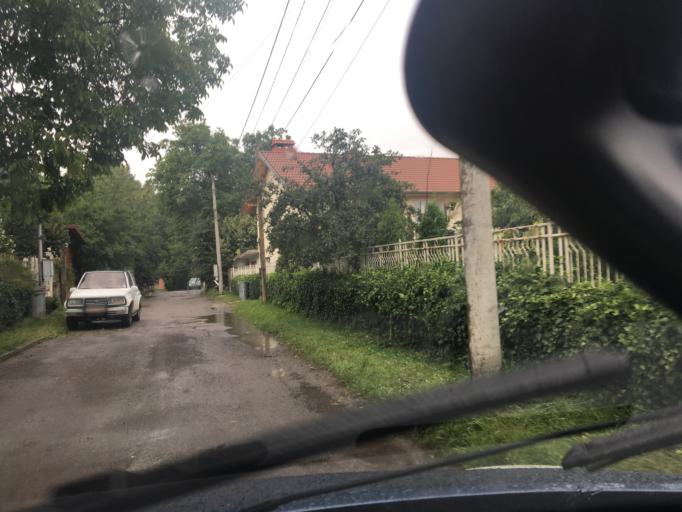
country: BG
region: Sofia-Capital
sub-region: Stolichna Obshtina
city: Sofia
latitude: 42.5860
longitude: 23.3506
